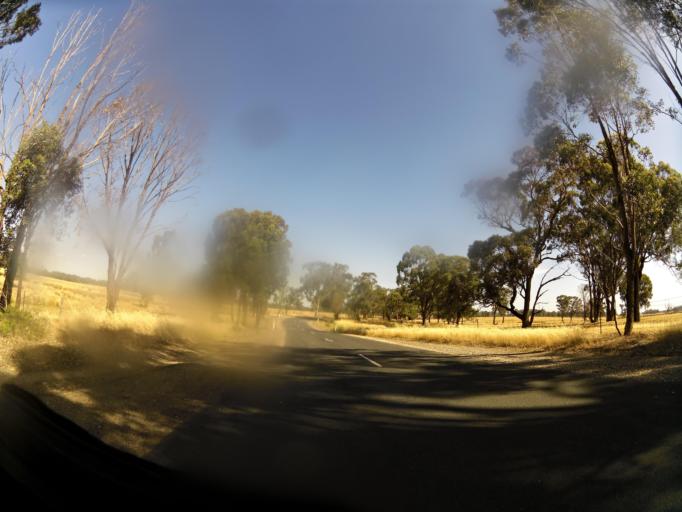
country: AU
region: Victoria
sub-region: Murrindindi
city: Kinglake West
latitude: -36.8957
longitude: 145.1069
